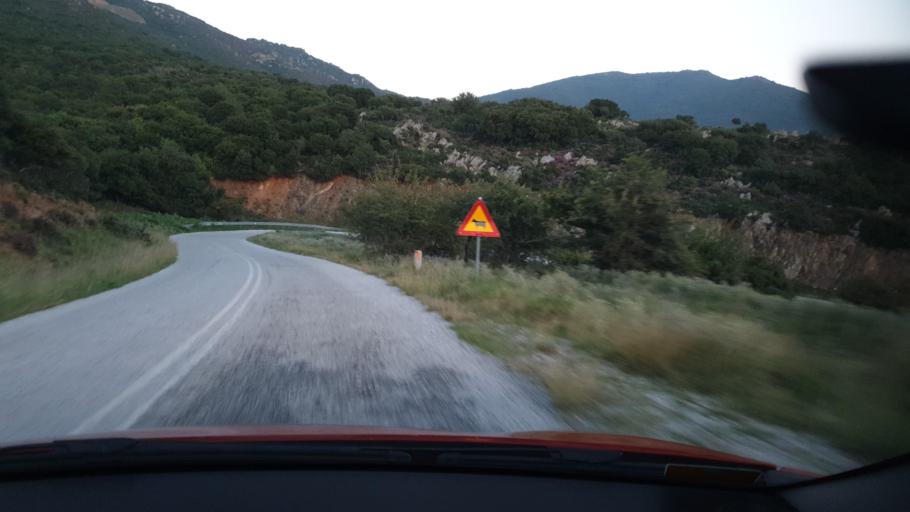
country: GR
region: Central Macedonia
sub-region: Nomos Thessalonikis
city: Peristera
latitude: 40.5202
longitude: 23.1875
